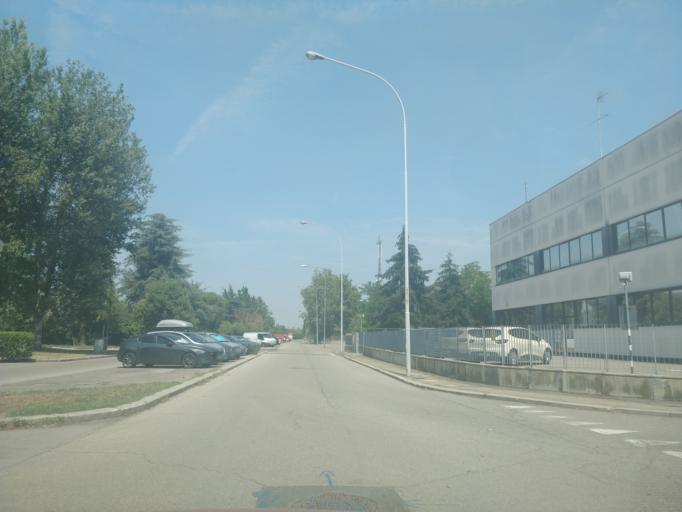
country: IT
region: Emilia-Romagna
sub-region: Provincia di Bologna
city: Progresso
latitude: 44.5609
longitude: 11.3710
